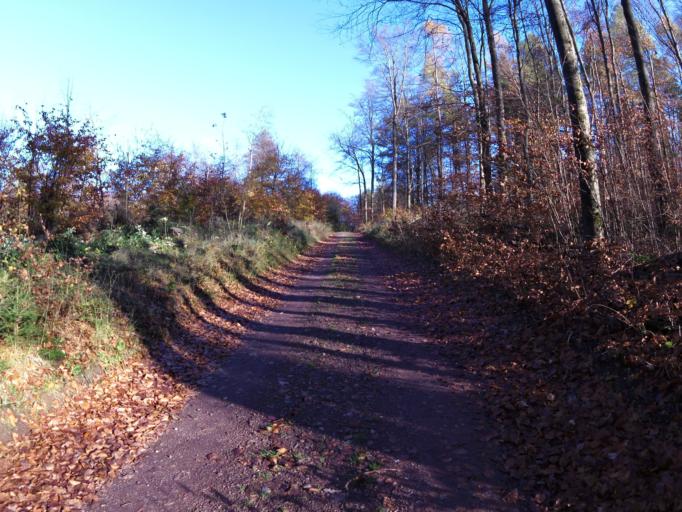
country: DE
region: Thuringia
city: Ruhla
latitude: 50.9071
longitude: 10.3383
